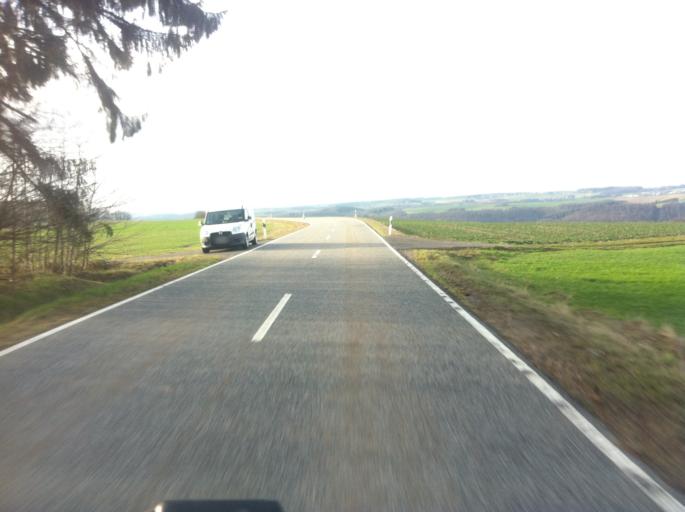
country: DE
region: Rheinland-Pfalz
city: Wurrich
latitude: 49.9758
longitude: 7.2889
